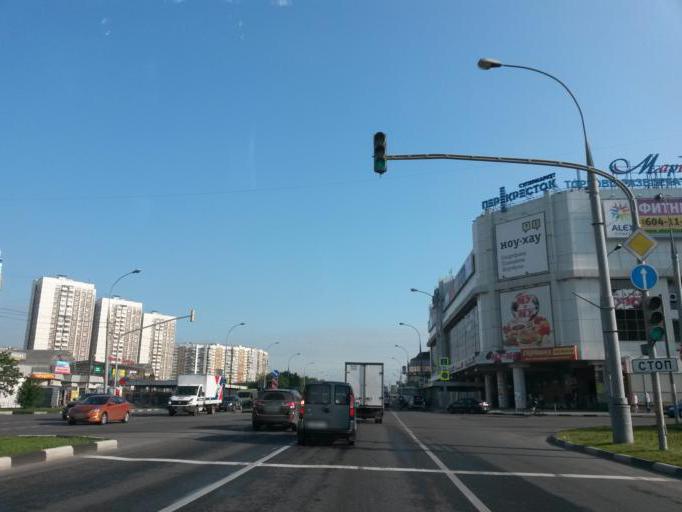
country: RU
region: Moscow
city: Brateyevo
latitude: 55.6482
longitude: 37.7447
